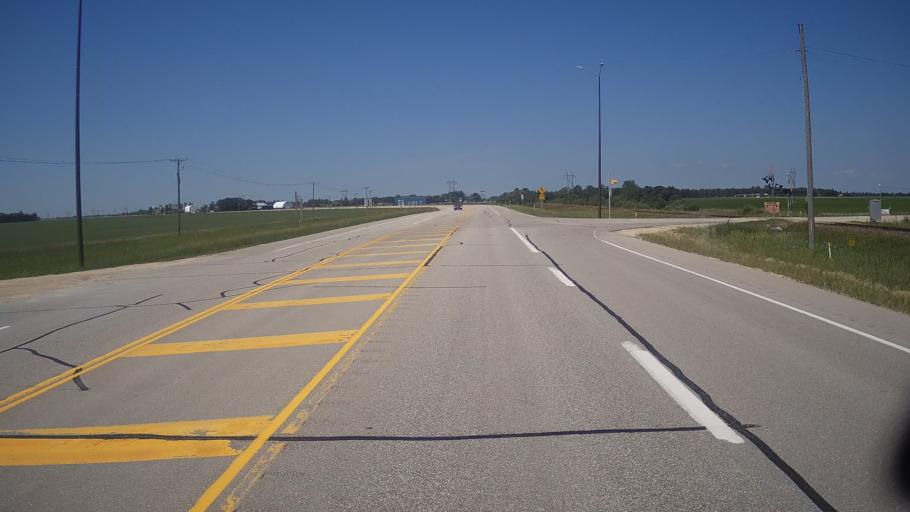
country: CA
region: Manitoba
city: Stonewall
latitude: 50.1200
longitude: -97.5279
